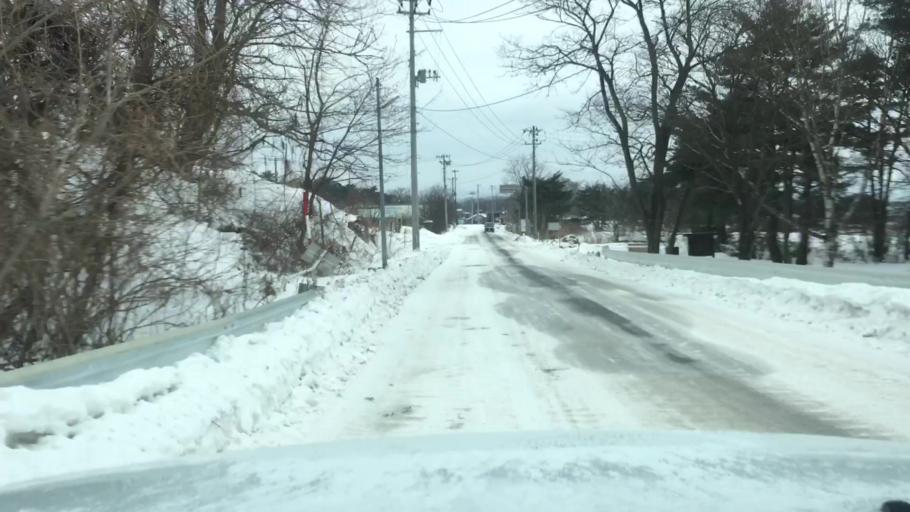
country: JP
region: Iwate
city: Shizukuishi
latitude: 39.9129
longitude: 141.0050
